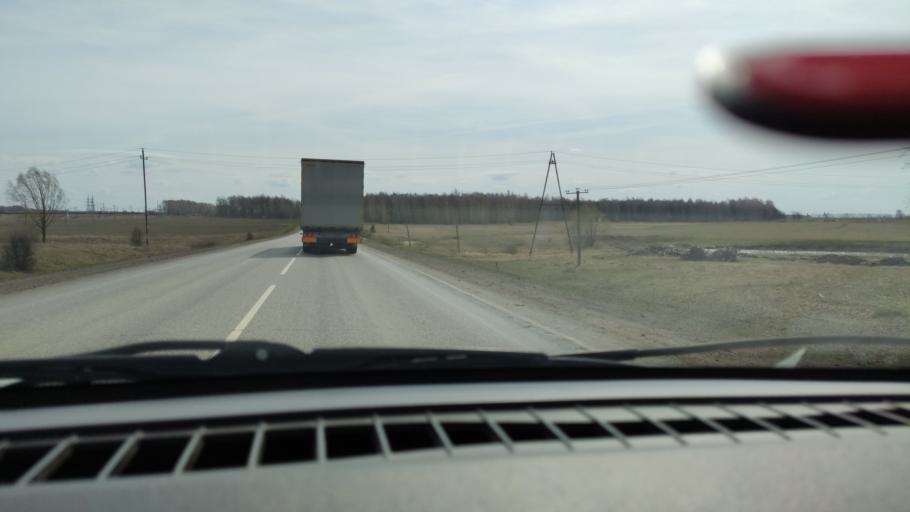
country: RU
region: Bashkortostan
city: Dyurtyuli
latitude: 55.3601
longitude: 54.9000
